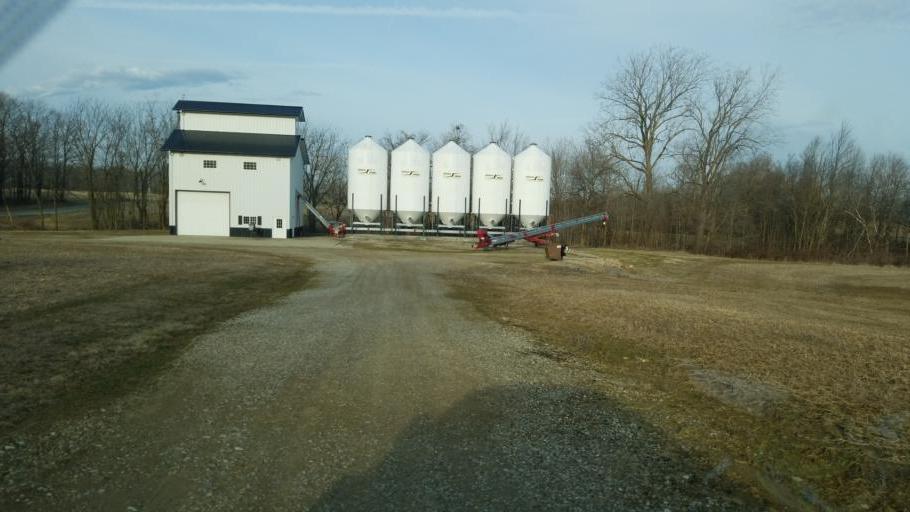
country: US
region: Ohio
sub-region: Knox County
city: Centerburg
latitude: 40.4209
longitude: -82.7085
